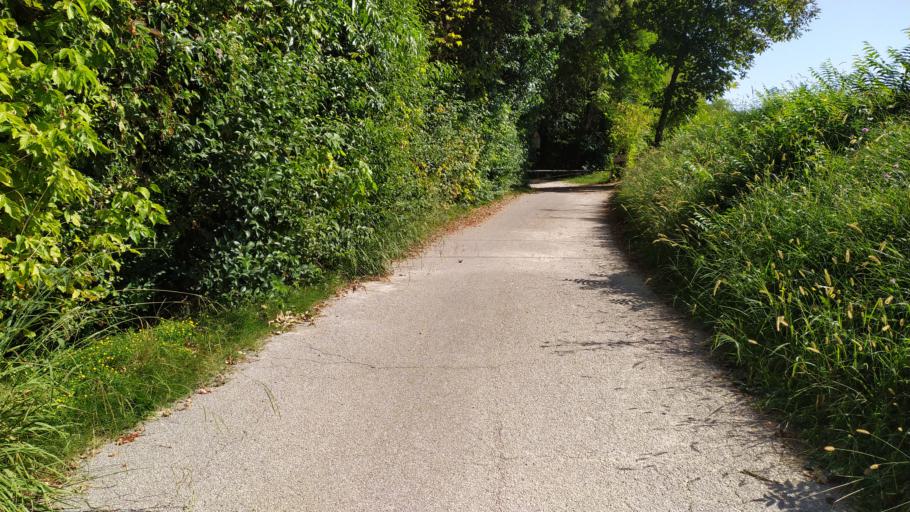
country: IT
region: Friuli Venezia Giulia
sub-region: Provincia di Pordenone
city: Cavolano-Schiavoi
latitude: 45.9386
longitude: 12.4891
